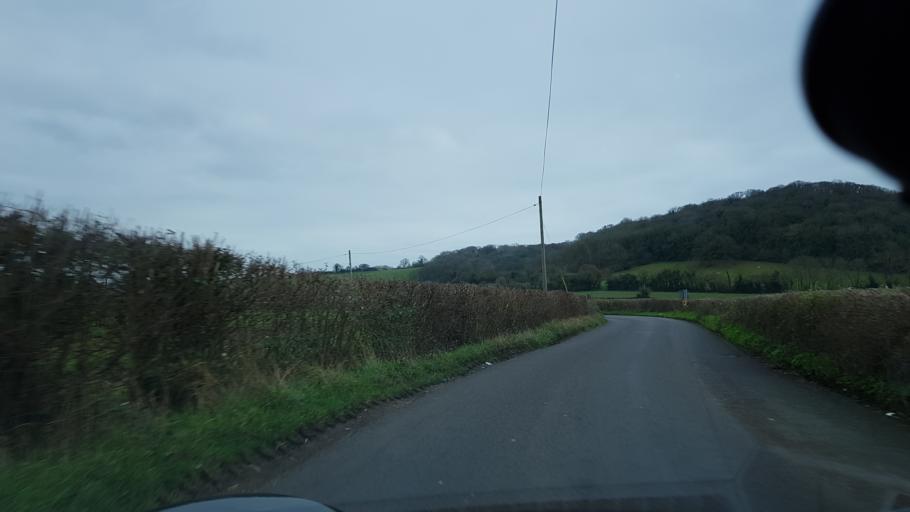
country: GB
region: England
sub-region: Somerset
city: Creech Saint Michael
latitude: 51.0067
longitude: -3.0517
